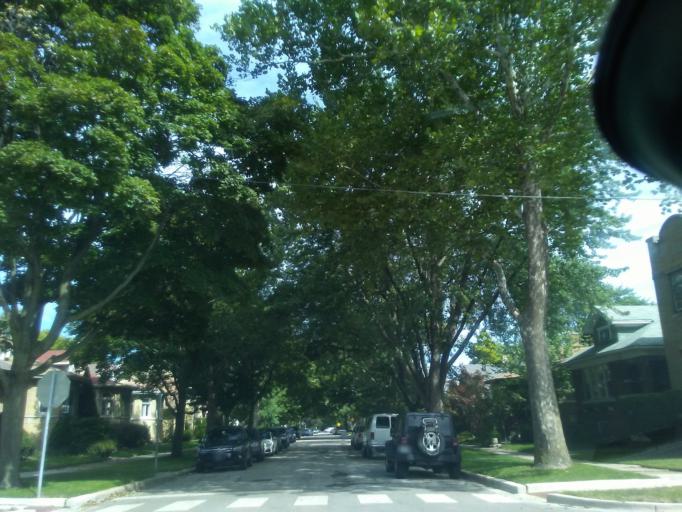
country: US
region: Illinois
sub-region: Cook County
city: Evanston
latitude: 42.0167
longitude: -87.6949
